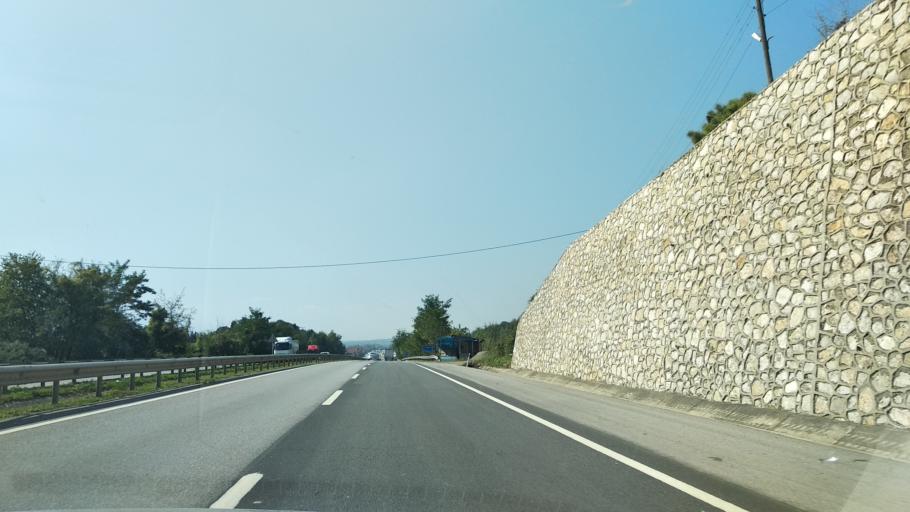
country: TR
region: Sakarya
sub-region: Merkez
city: Sapanca
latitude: 40.7352
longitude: 30.2347
